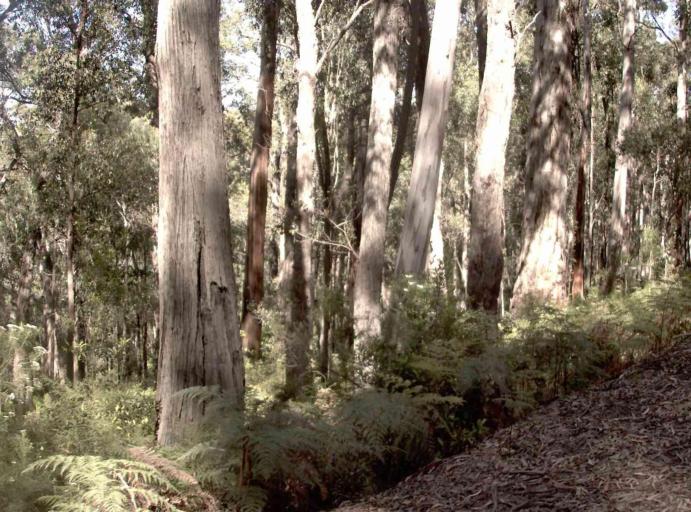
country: AU
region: New South Wales
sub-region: Bombala
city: Bombala
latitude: -37.2612
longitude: 148.7296
